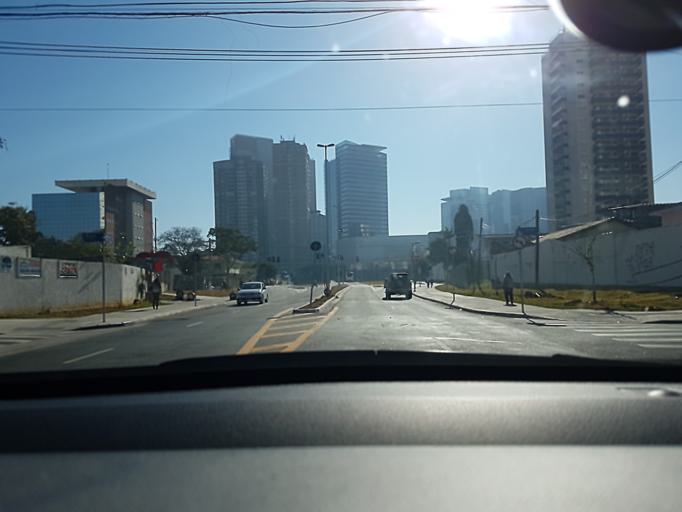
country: BR
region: Sao Paulo
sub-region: Taboao Da Serra
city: Taboao da Serra
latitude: -23.6289
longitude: -46.7083
